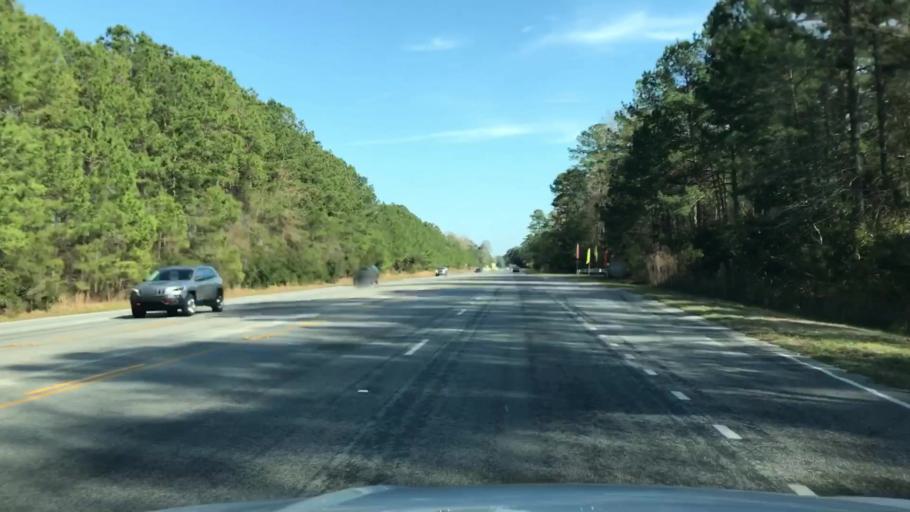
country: US
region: South Carolina
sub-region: Beaufort County
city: Bluffton
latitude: 32.3540
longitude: -80.9060
